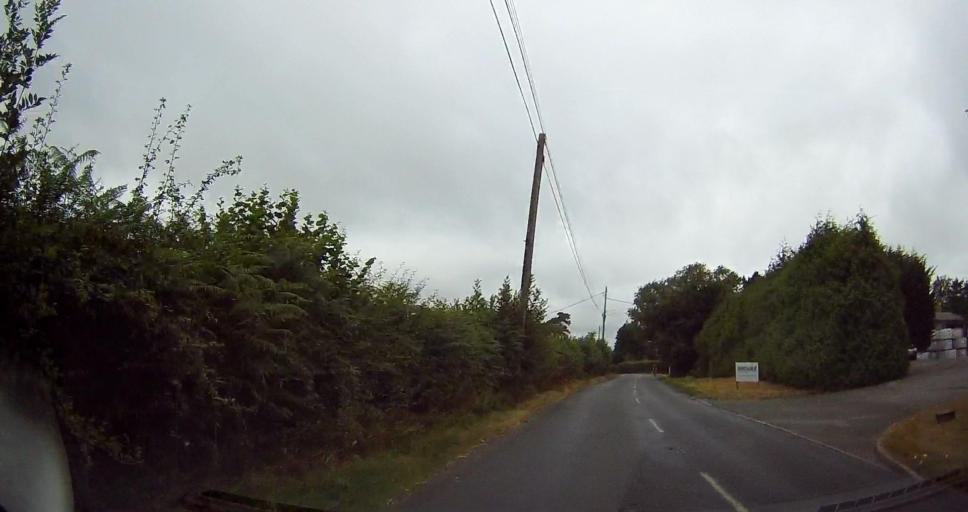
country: GB
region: England
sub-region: East Sussex
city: Wadhurst
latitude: 51.0787
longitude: 0.3651
